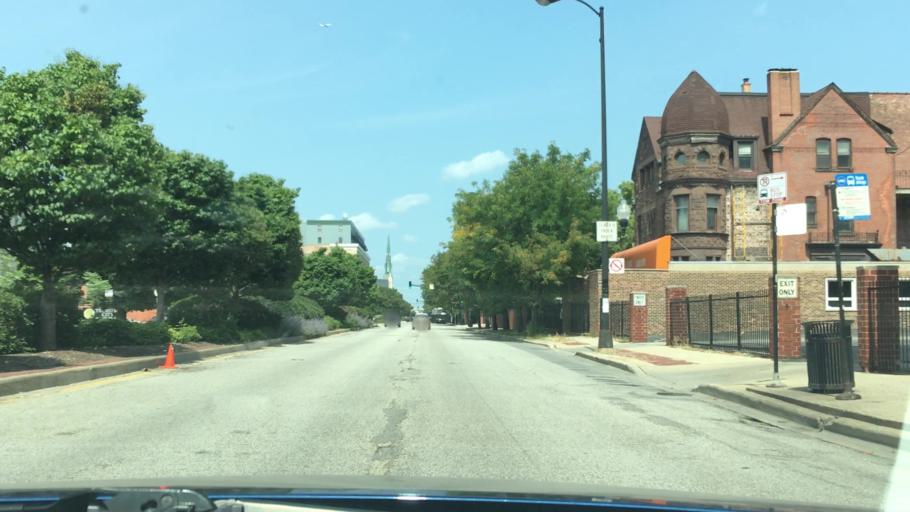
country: US
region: Illinois
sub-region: Cook County
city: Chicago
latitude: 41.8766
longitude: -87.6666
